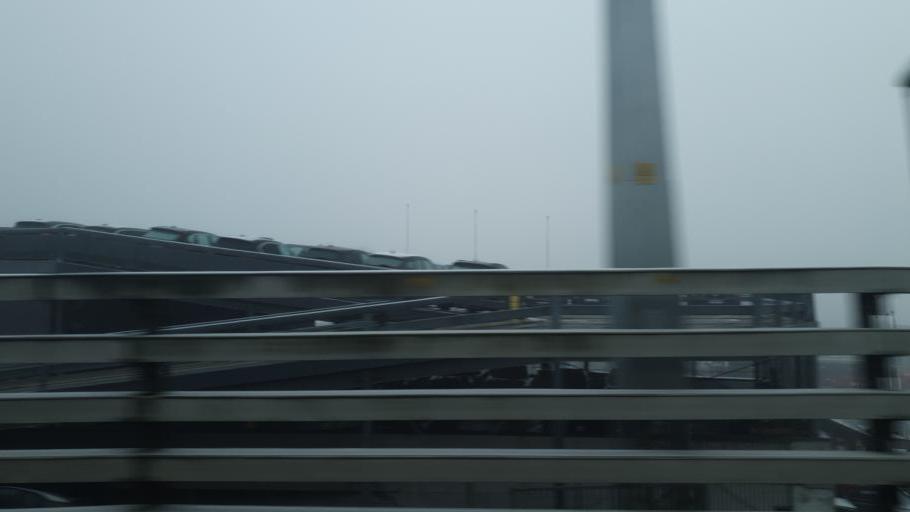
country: NO
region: Oslo
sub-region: Oslo
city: Sjolyststranda
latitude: 59.9181
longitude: 10.6596
